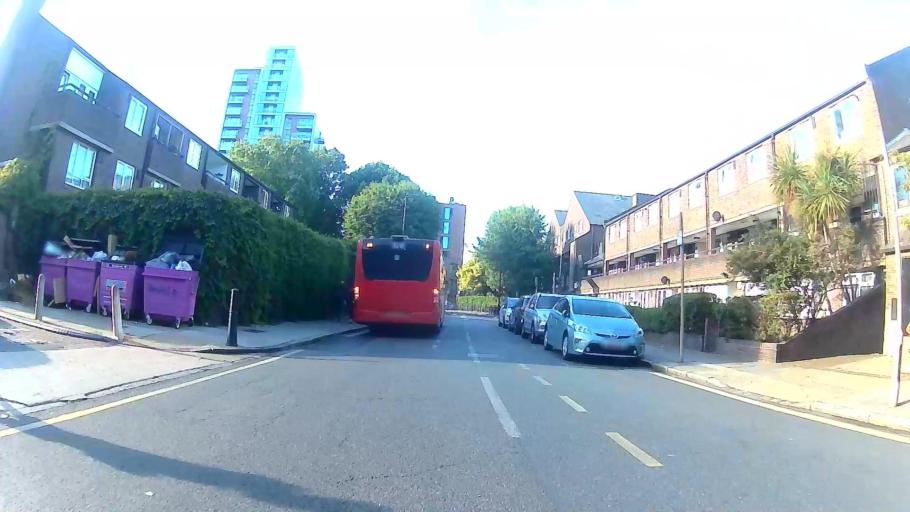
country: GB
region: England
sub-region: Greater London
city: Poplar
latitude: 51.5229
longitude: -0.0186
